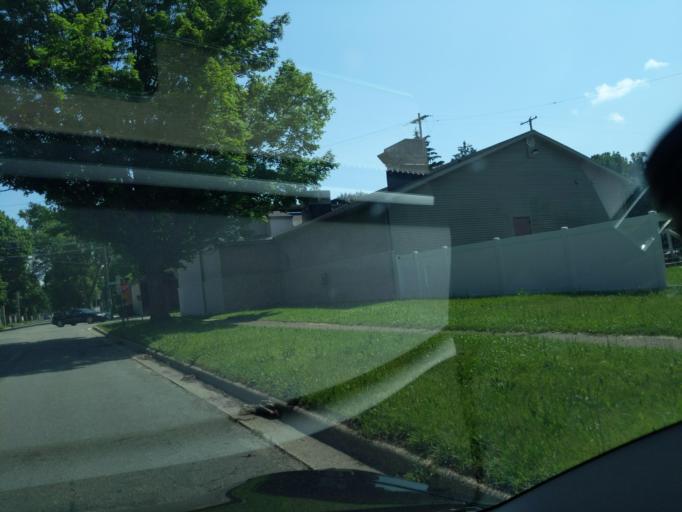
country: US
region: Michigan
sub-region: Jackson County
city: Jackson
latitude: 42.2594
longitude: -84.4120
